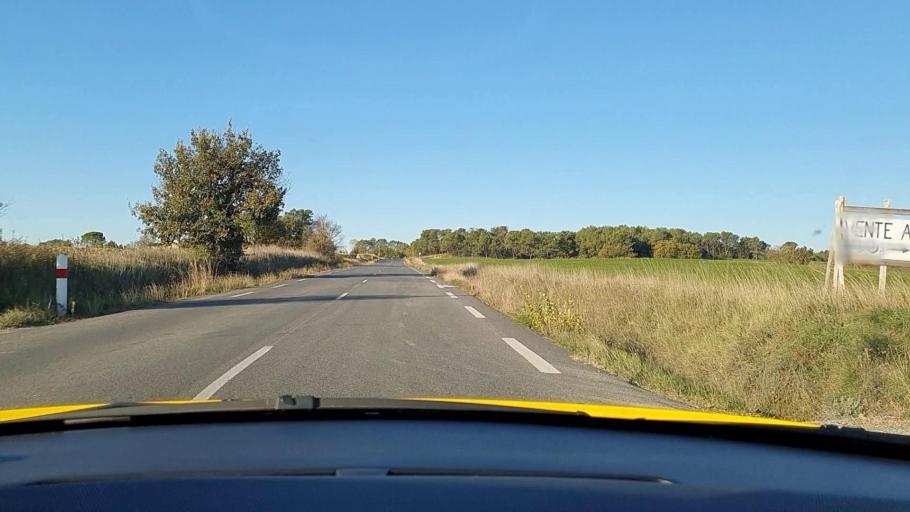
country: FR
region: Languedoc-Roussillon
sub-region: Departement du Gard
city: Salindres
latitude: 44.1884
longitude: 4.2062
